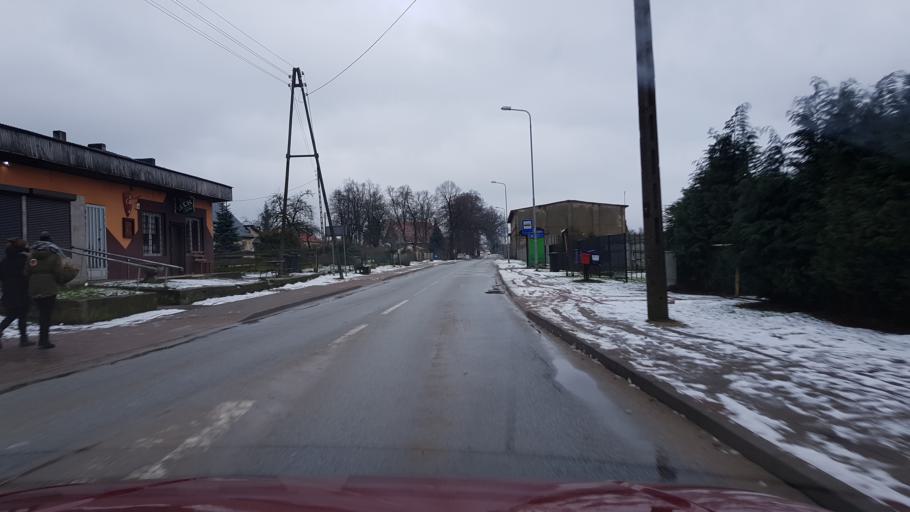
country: PL
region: West Pomeranian Voivodeship
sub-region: Powiat gryficki
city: Ploty
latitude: 53.7065
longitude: 15.2738
